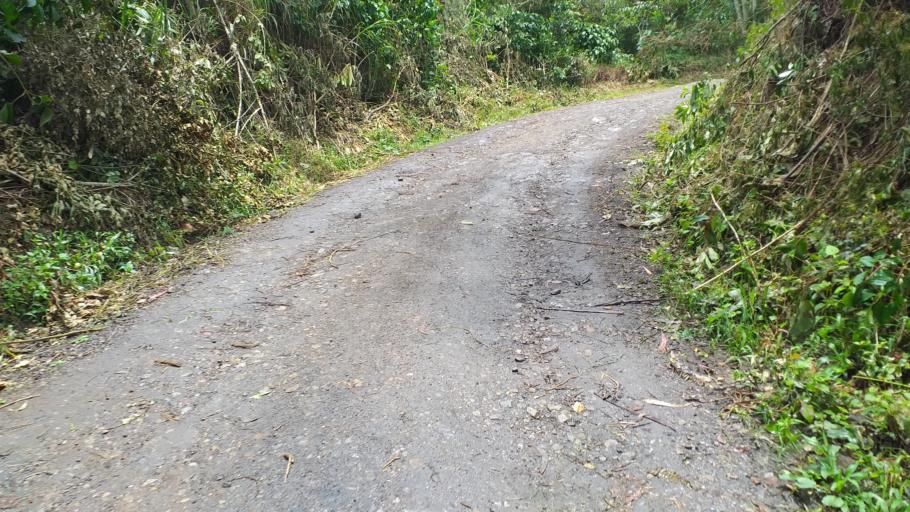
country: CO
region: Cundinamarca
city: Tenza
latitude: 5.1129
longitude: -73.4525
